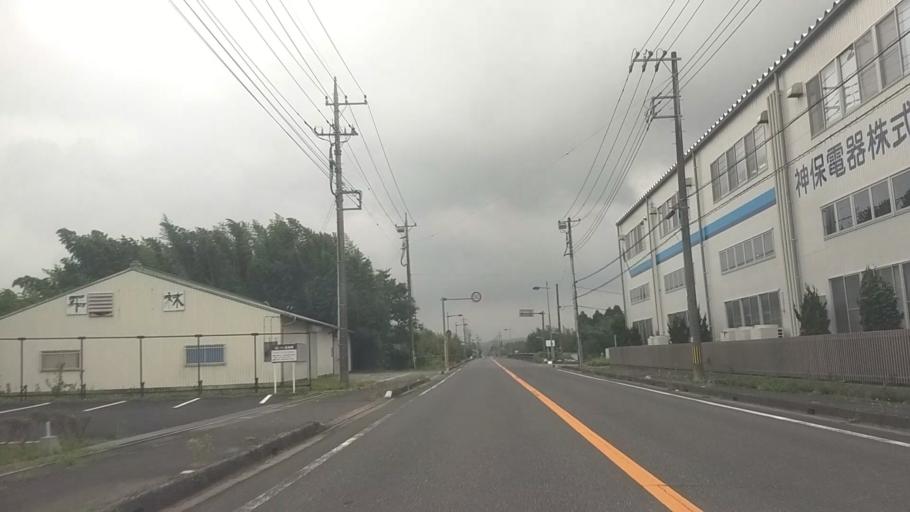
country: JP
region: Chiba
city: Ohara
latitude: 35.2861
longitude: 140.2644
